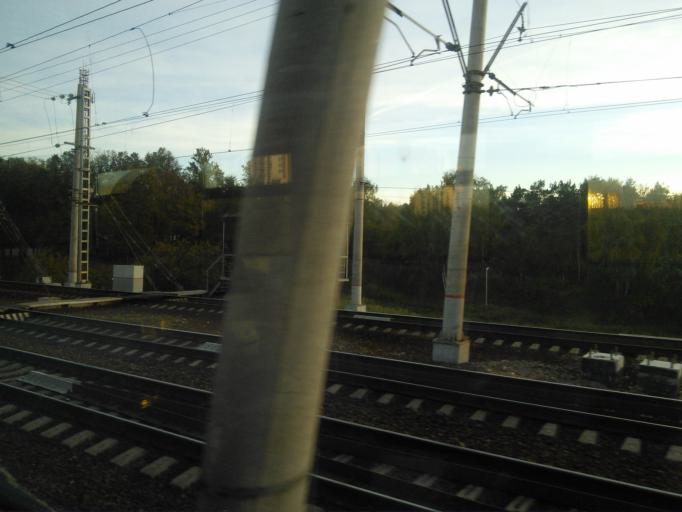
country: RU
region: Moskovskaya
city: Levoberezhnaya
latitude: 55.8892
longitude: 37.4641
